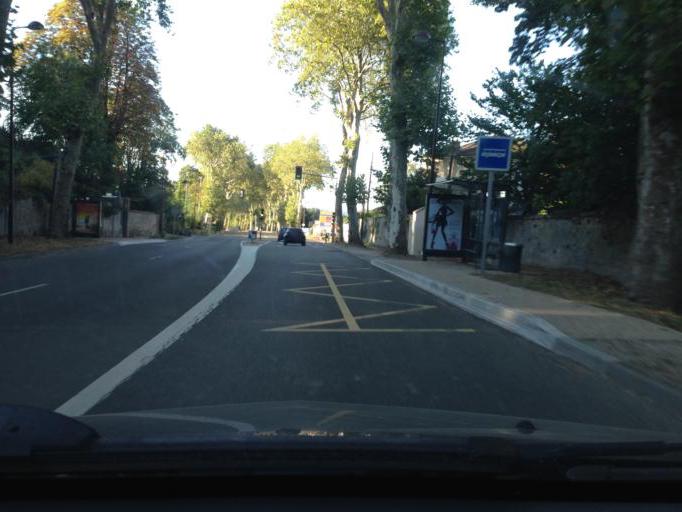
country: FR
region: Ile-de-France
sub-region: Departement des Yvelines
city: Louveciennes
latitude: 48.8655
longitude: 2.1128
